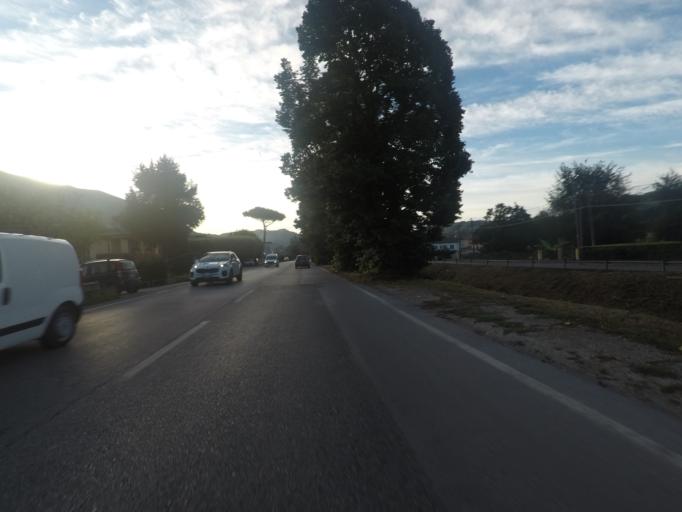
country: IT
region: Tuscany
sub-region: Provincia di Lucca
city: Corsanico-Bargecchia
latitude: 43.9336
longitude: 10.3080
